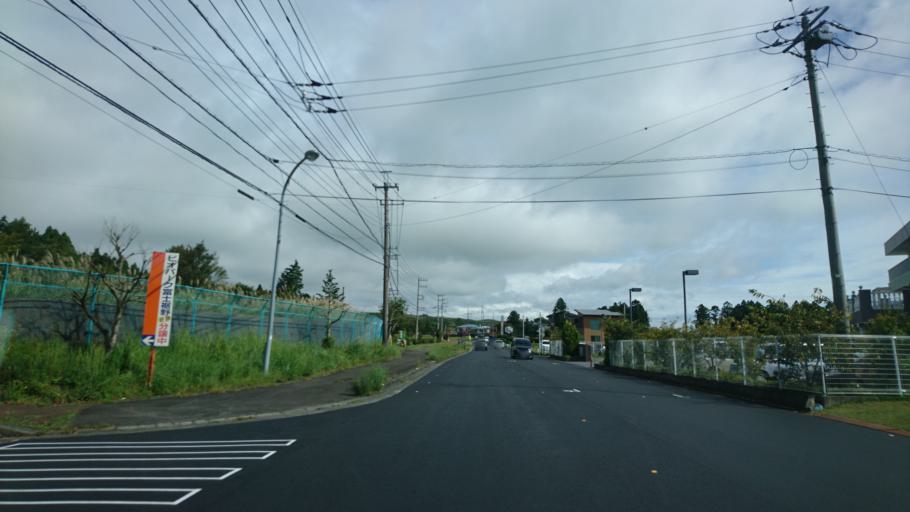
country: JP
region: Shizuoka
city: Gotemba
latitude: 35.2580
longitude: 138.8598
